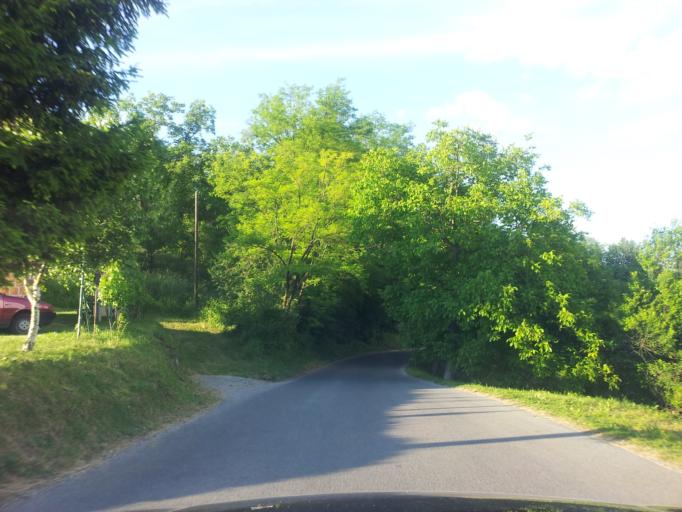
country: HR
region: Karlovacka
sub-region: Grad Karlovac
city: Karlovac
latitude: 45.4819
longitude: 15.4813
